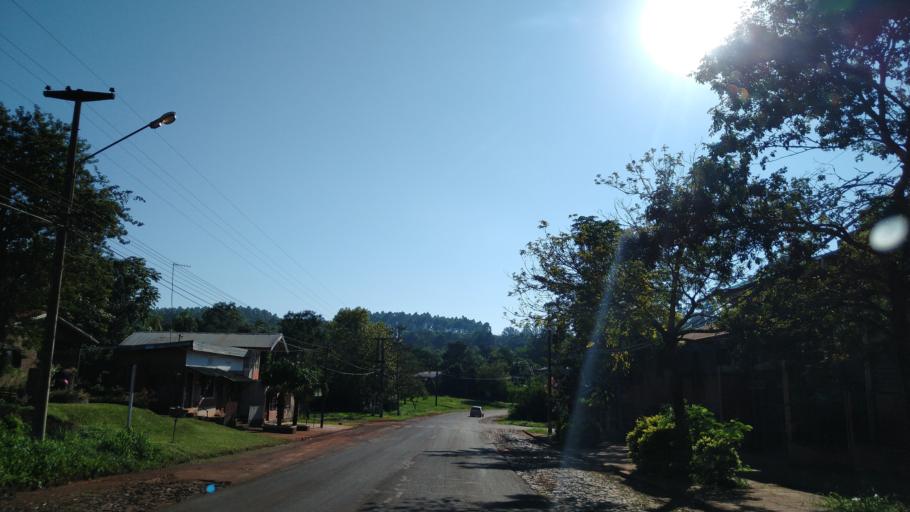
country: AR
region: Misiones
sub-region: Departamento de Montecarlo
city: Montecarlo
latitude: -26.5616
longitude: -54.7816
